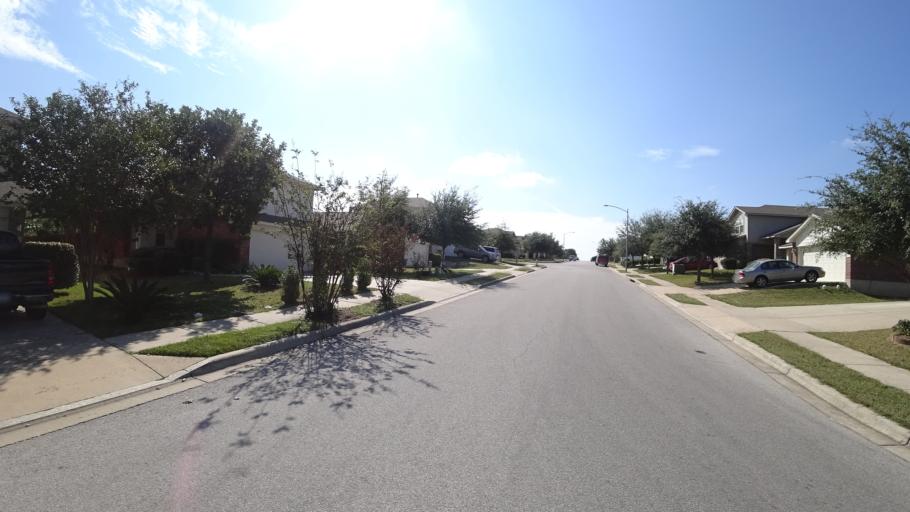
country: US
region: Texas
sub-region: Travis County
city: Pflugerville
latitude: 30.4217
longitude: -97.6312
